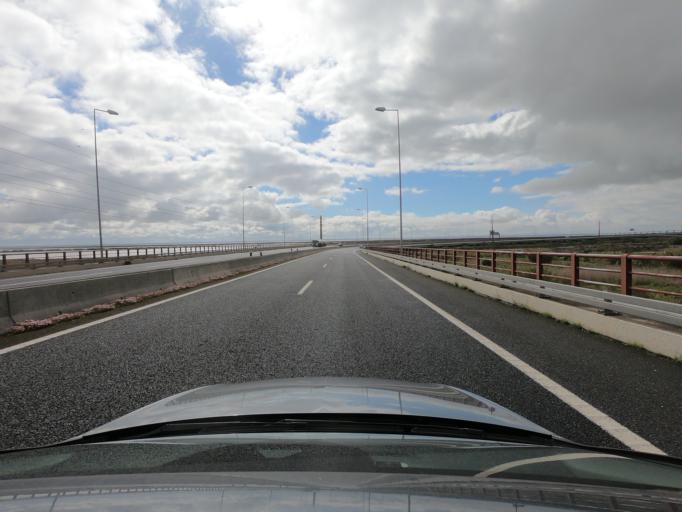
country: PT
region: Lisbon
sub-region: Loures
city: Santa Iria da Azoia
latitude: 38.8437
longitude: -9.0755
